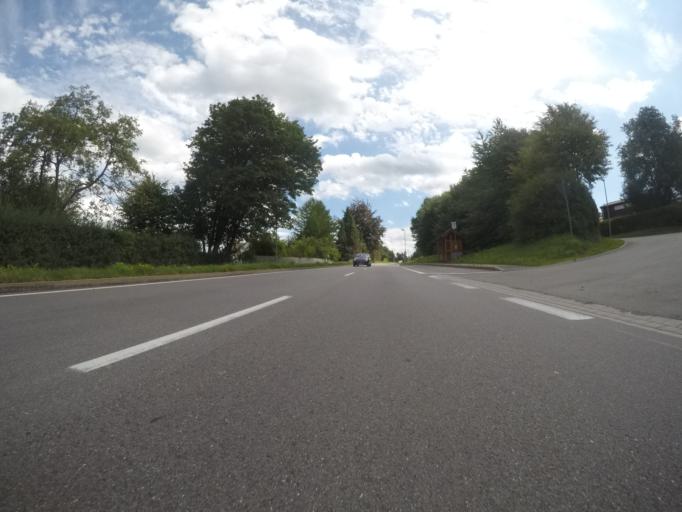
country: DE
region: Baden-Wuerttemberg
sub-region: Karlsruhe Region
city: Oberreichenbach
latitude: 48.7321
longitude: 8.6651
